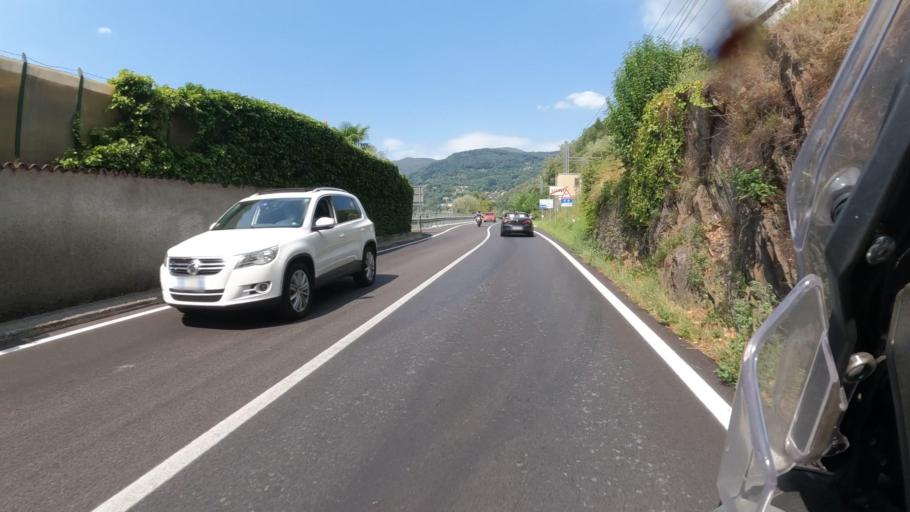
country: IT
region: Lombardy
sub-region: Provincia di Varese
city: Luino
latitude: 46.0089
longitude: 8.7483
